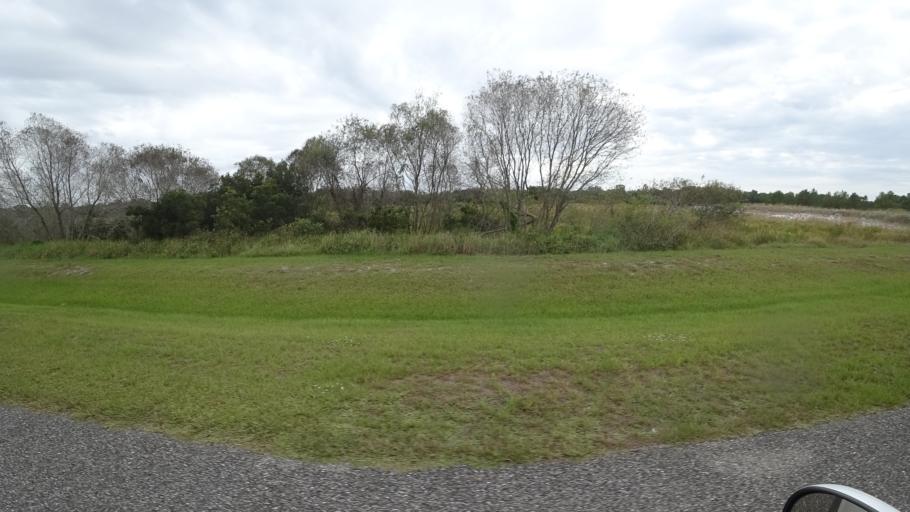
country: US
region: Florida
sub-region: Hillsborough County
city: Wimauma
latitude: 27.6487
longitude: -82.3260
